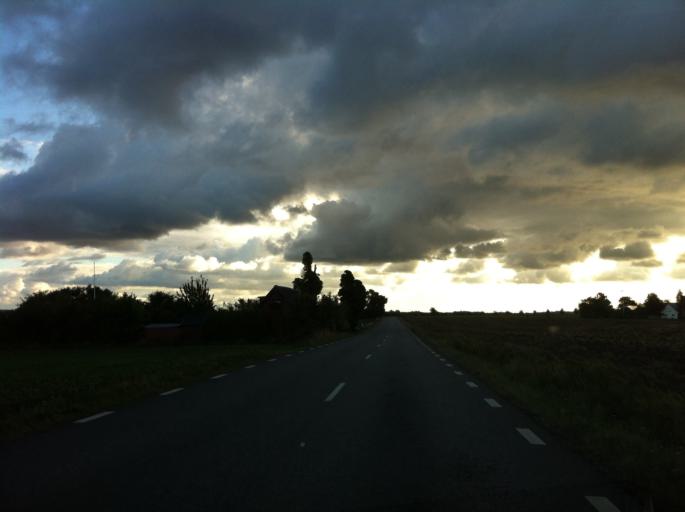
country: SE
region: Skane
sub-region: Svalovs Kommun
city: Svaloev
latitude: 55.8881
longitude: 13.1760
